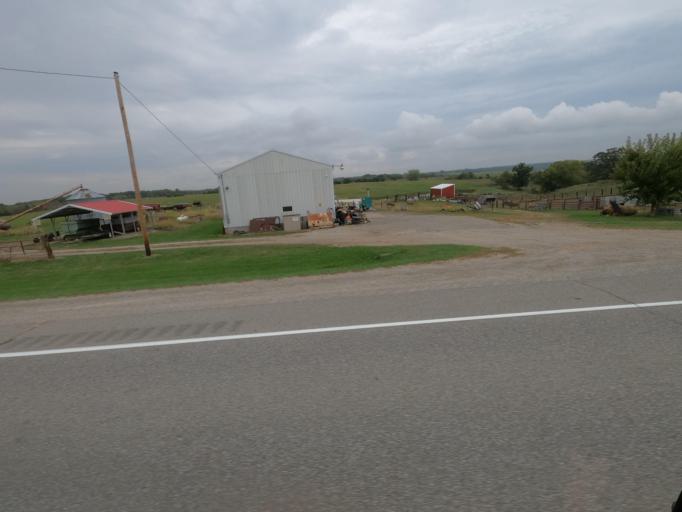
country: US
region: Iowa
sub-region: Van Buren County
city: Keosauqua
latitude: 40.8322
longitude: -91.9492
